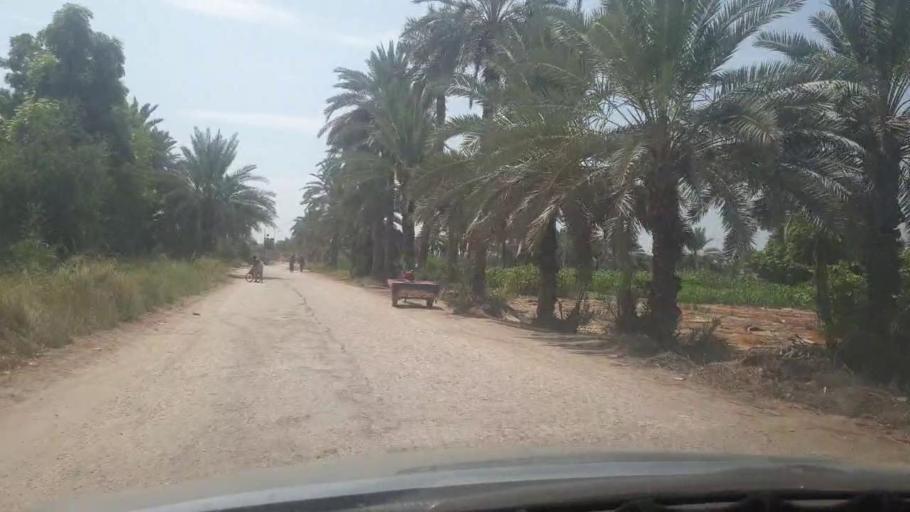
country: PK
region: Sindh
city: Bozdar
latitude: 27.1961
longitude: 68.5867
